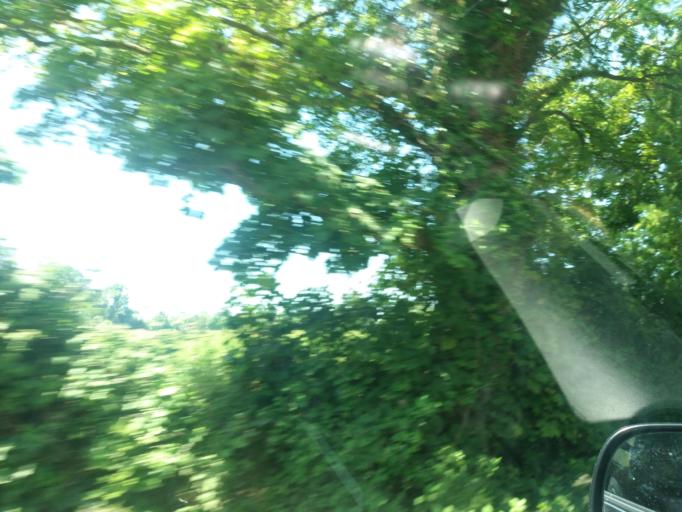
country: IE
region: Leinster
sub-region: Fingal County
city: Swords
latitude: 53.5157
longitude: -6.2358
